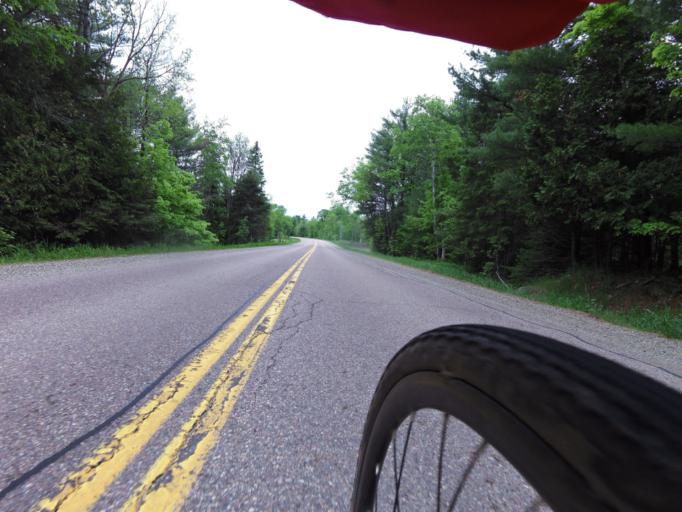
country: CA
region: Ontario
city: Renfrew
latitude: 45.2884
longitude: -76.6864
